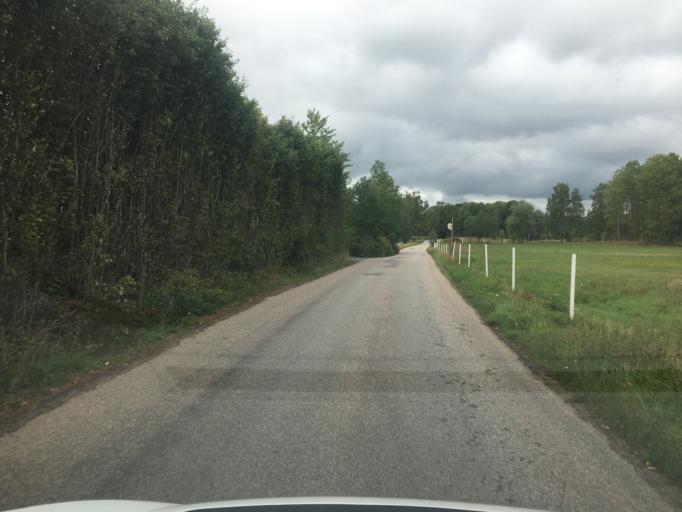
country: SE
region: Kronoberg
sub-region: Ljungby Kommun
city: Lagan
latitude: 56.9254
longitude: 14.0204
